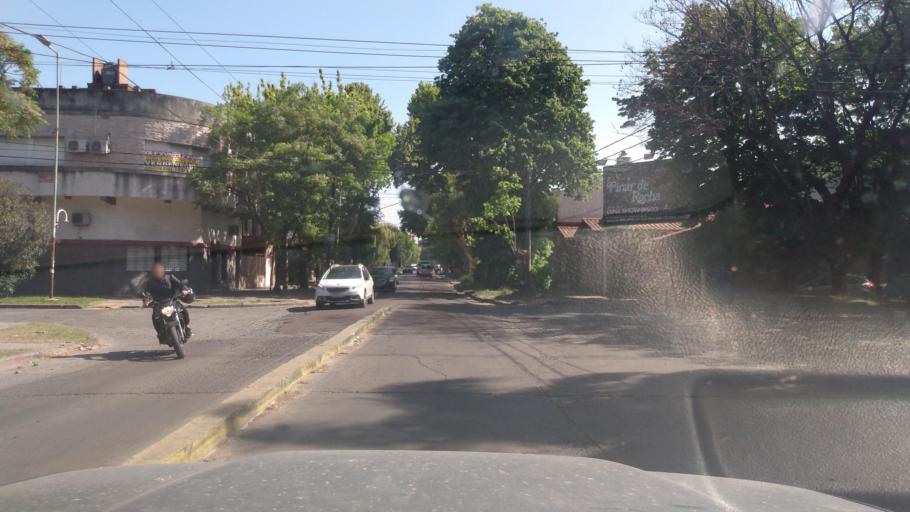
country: AR
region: Buenos Aires
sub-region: Partido de Moron
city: Moron
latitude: -34.6439
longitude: -58.5951
